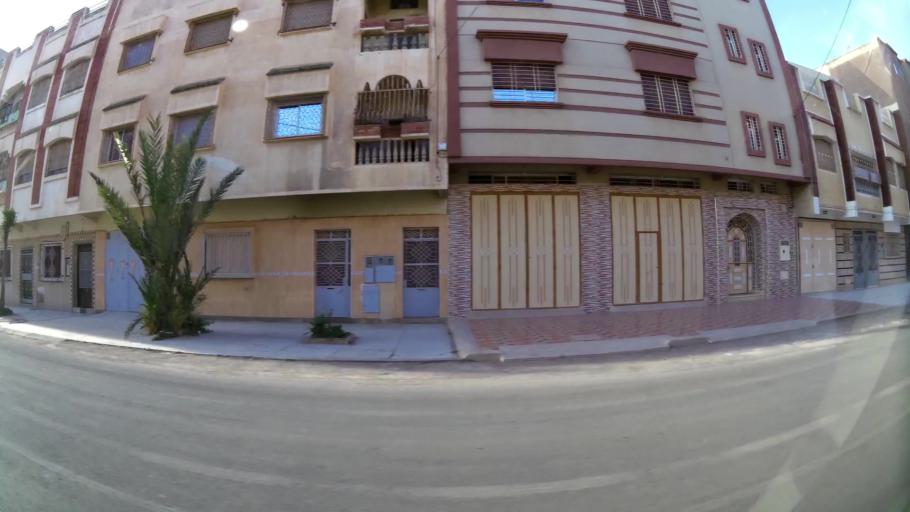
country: MA
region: Oriental
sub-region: Oujda-Angad
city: Oujda
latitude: 34.6775
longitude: -1.8973
